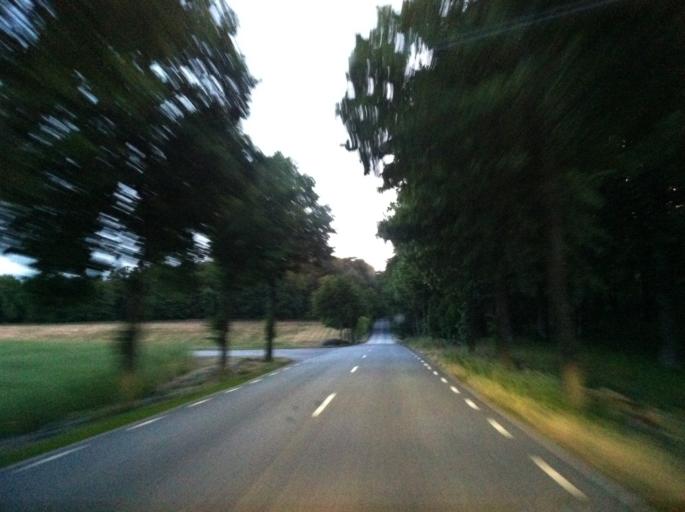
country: SE
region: Skane
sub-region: Tomelilla Kommun
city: Tomelilla
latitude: 55.5677
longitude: 13.8773
